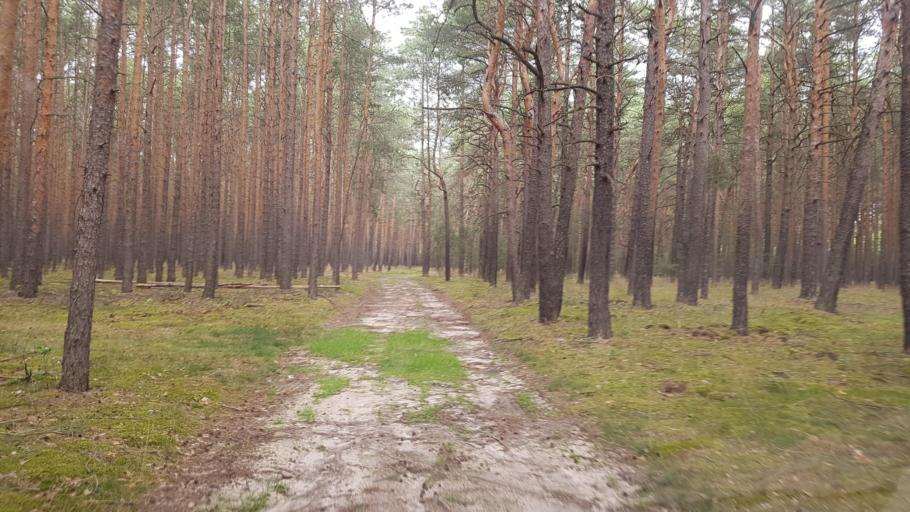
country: DE
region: Brandenburg
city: Crinitz
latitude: 51.7107
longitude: 13.7278
